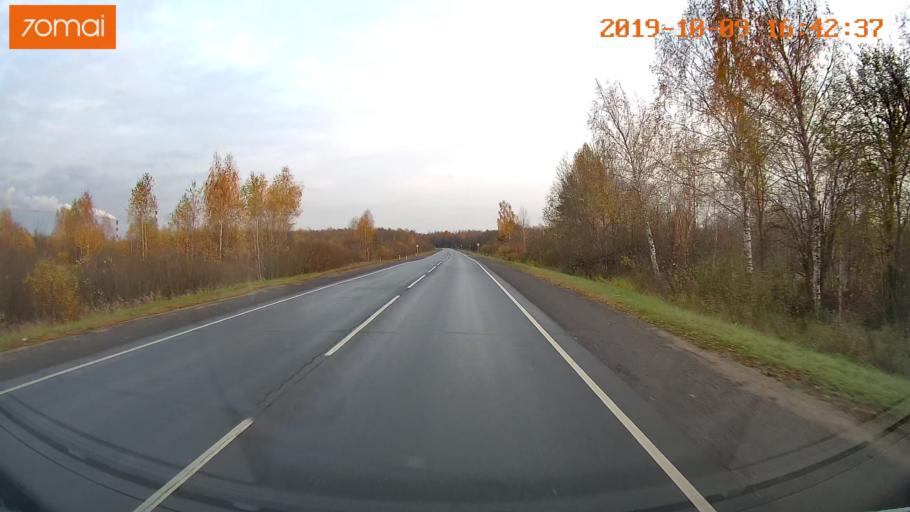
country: RU
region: Kostroma
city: Volgorechensk
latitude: 57.4601
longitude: 41.1041
